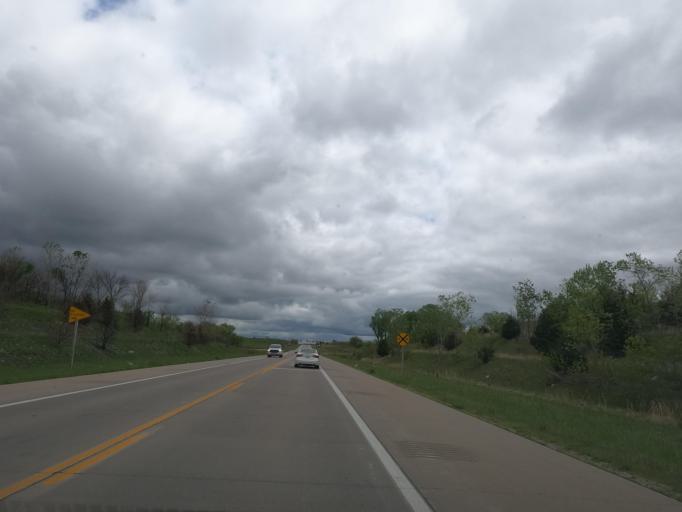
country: US
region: Kansas
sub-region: Montgomery County
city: Cherryvale
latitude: 37.3482
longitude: -95.5974
